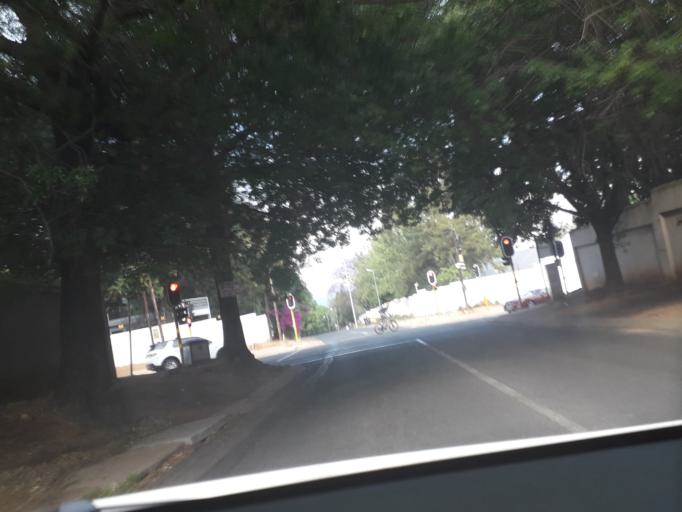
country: ZA
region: Gauteng
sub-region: City of Johannesburg Metropolitan Municipality
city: Diepsloot
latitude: -26.0670
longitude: 27.9956
